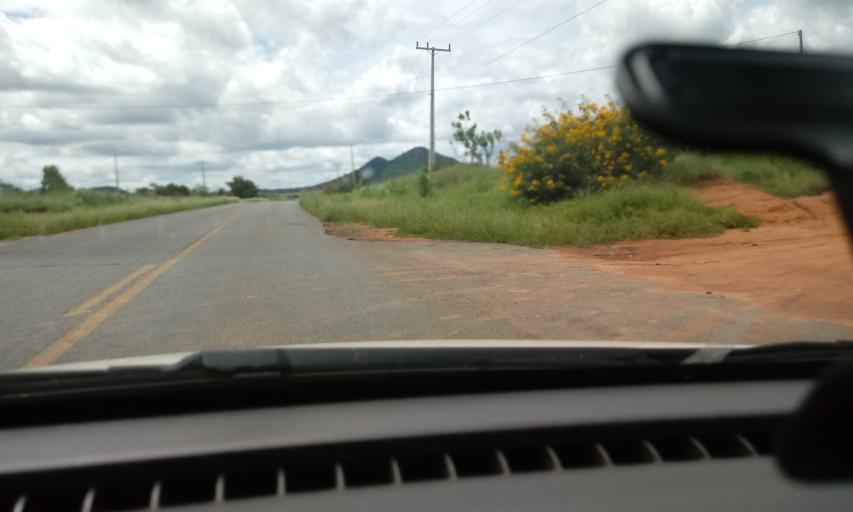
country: BR
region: Bahia
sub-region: Guanambi
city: Guanambi
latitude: -14.0850
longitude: -42.8760
